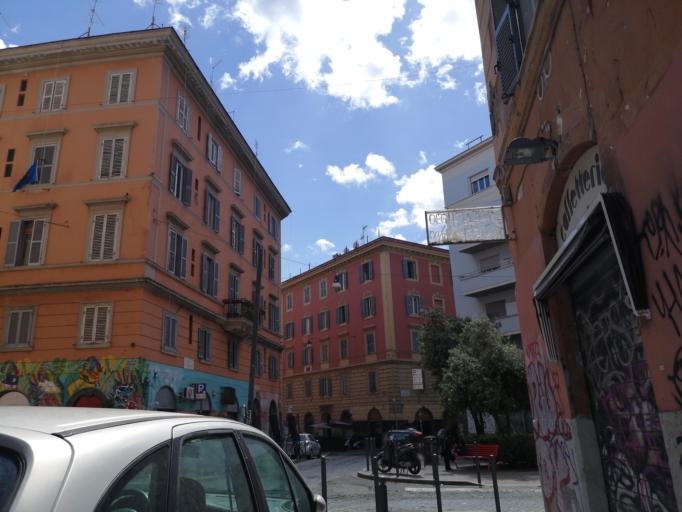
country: IT
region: Latium
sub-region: Citta metropolitana di Roma Capitale
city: Rome
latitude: 41.8955
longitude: 12.5139
